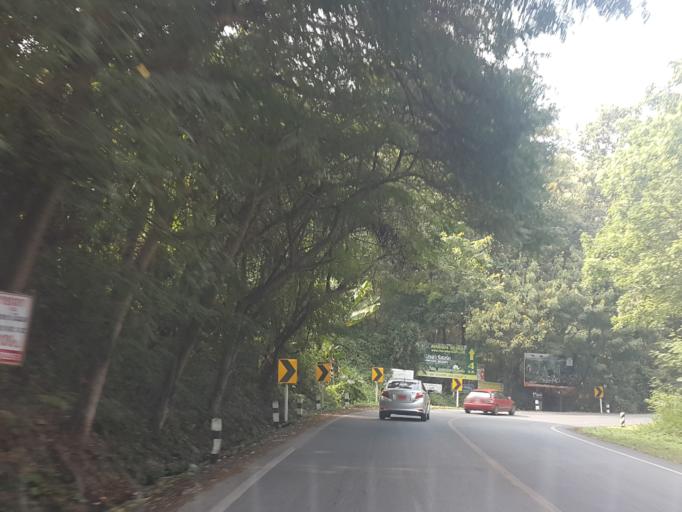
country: TH
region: Chiang Mai
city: Chiang Mai
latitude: 18.9076
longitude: 98.9016
